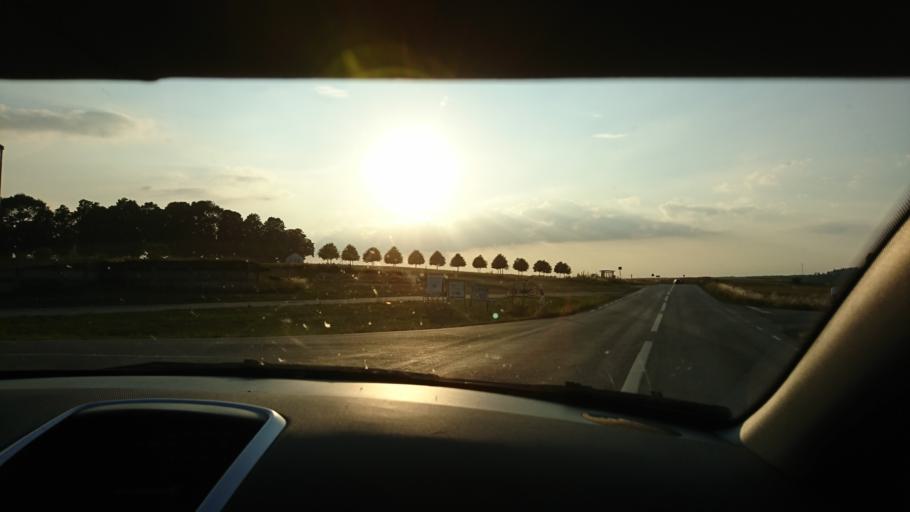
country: SE
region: Skane
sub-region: Simrishamns Kommun
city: Kivik
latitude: 55.7142
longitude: 14.1550
